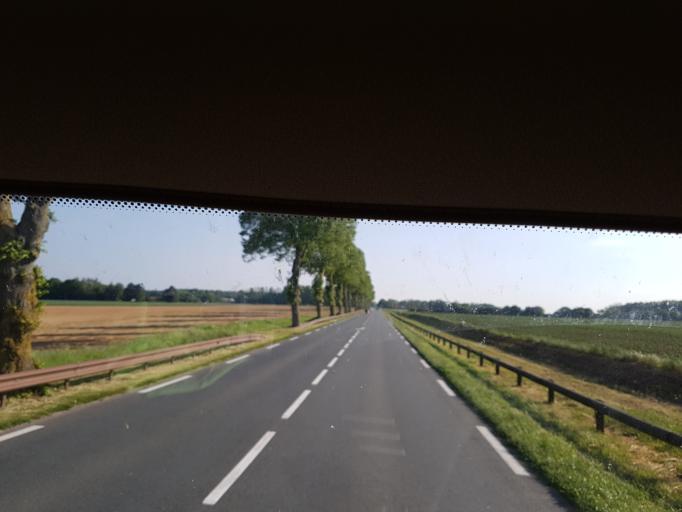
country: FR
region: Picardie
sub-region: Departement de la Somme
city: Abbeville
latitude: 50.1642
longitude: 1.8612
